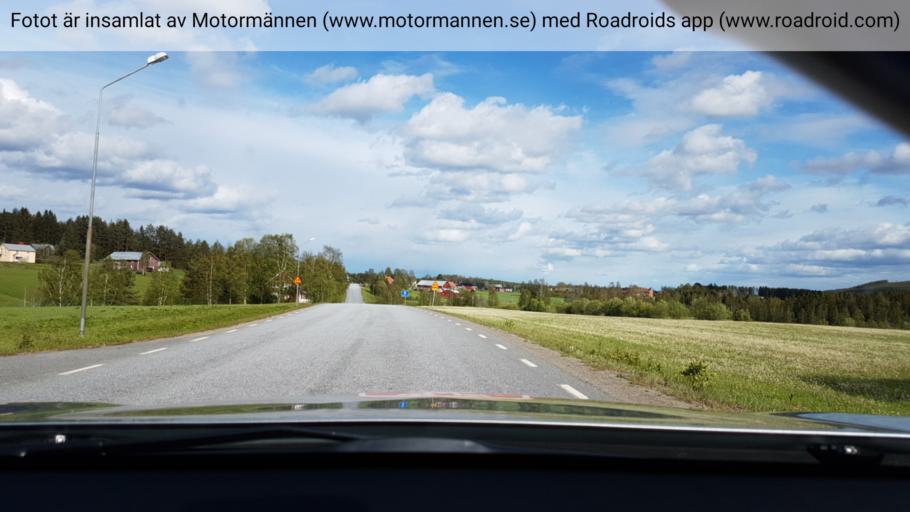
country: SE
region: Vaesterbotten
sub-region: Bjurholms Kommun
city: Bjurholm
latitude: 63.9253
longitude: 19.0423
